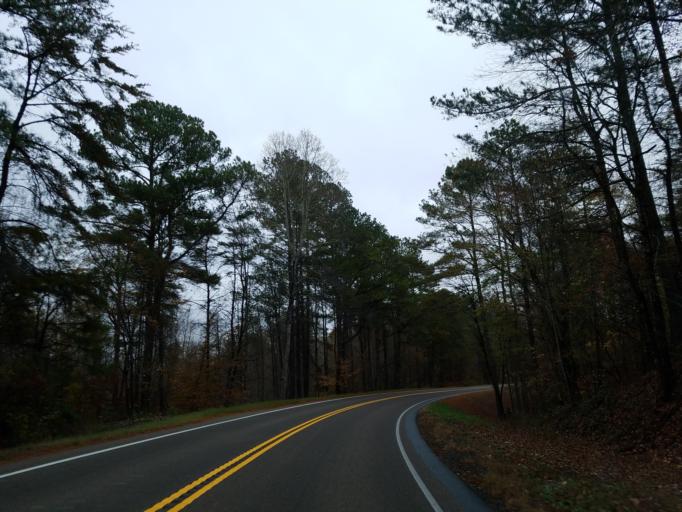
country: US
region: Georgia
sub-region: Cherokee County
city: Canton
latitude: 34.2823
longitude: -84.5740
